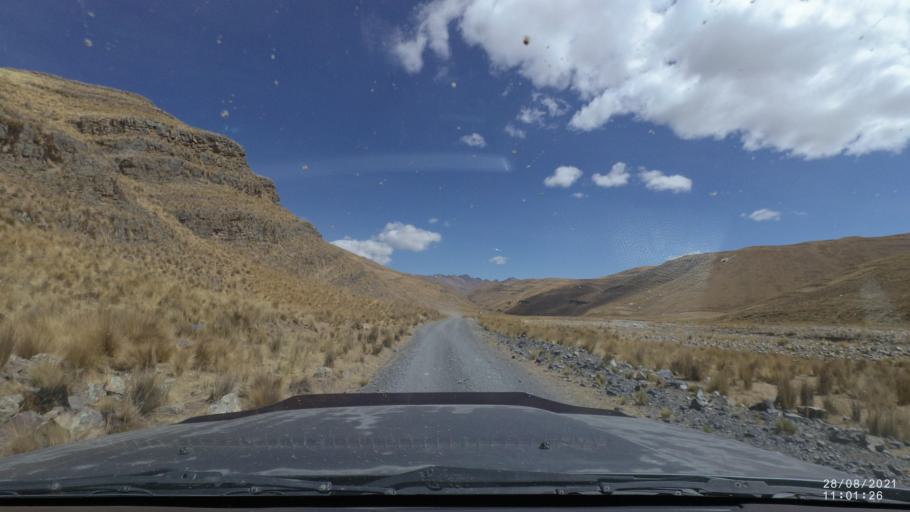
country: BO
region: Cochabamba
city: Cochabamba
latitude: -17.1810
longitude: -66.2662
